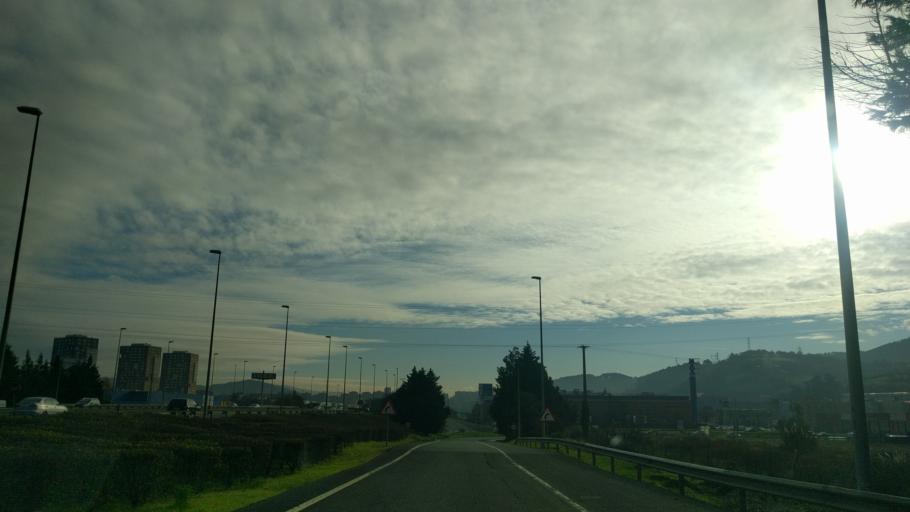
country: ES
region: Basque Country
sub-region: Bizkaia
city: Barakaldo
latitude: 43.2917
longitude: -3.0128
